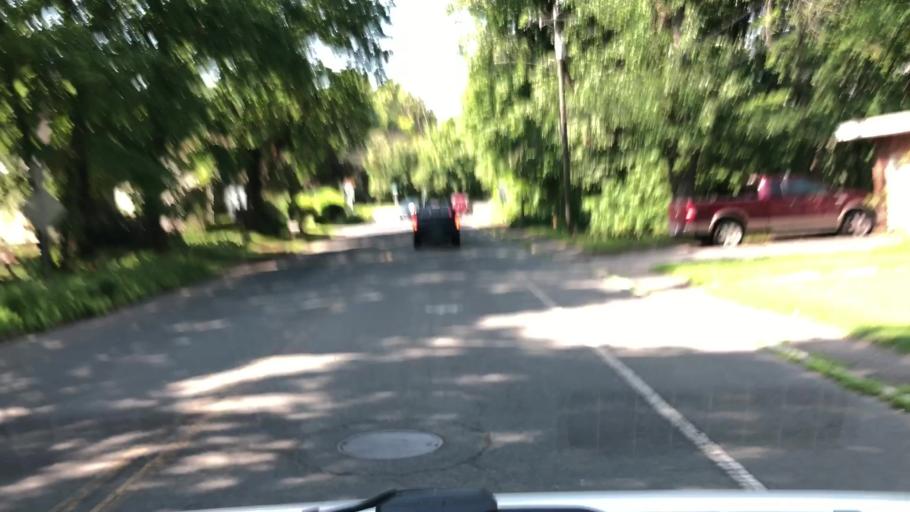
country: US
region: Massachusetts
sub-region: Franklin County
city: Greenfield
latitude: 42.5788
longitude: -72.5801
